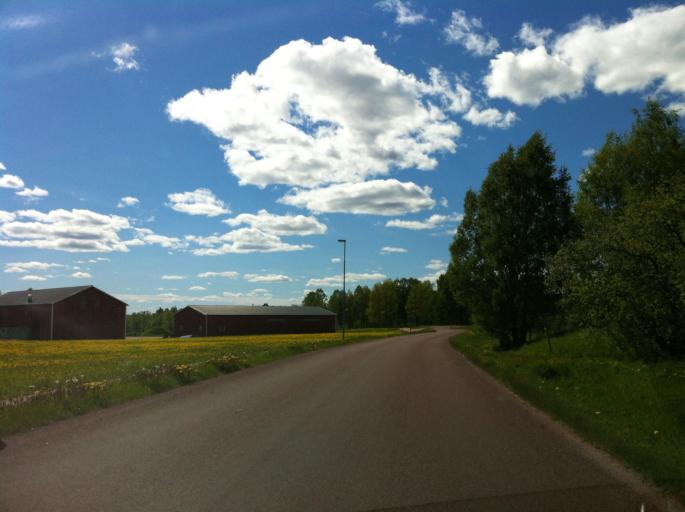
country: SE
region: Dalarna
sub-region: Mora Kommun
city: Mora
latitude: 61.0052
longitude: 14.6078
